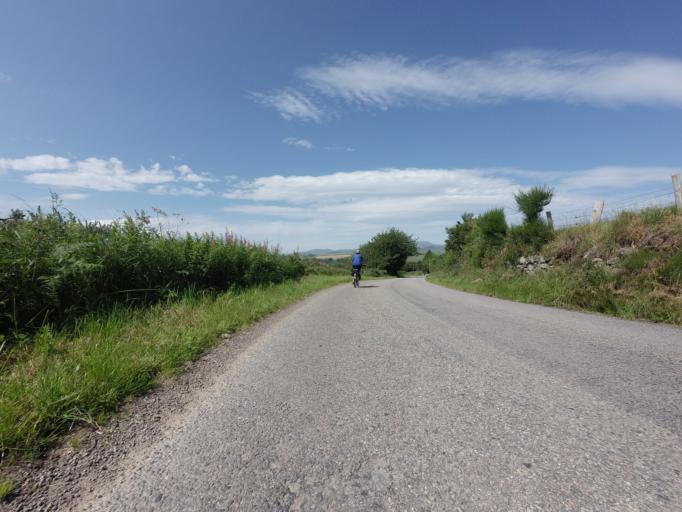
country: GB
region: Scotland
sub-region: Highland
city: Conon Bridge
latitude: 57.5625
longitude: -4.4188
